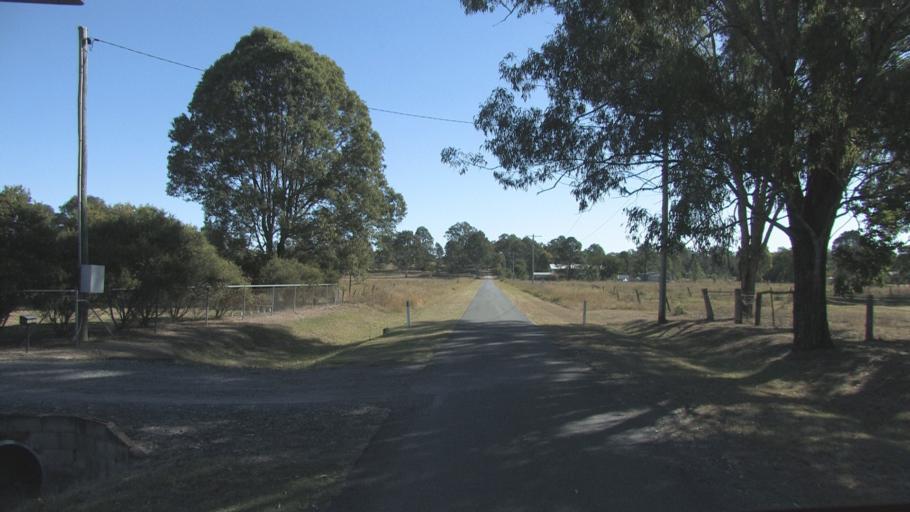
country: AU
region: Queensland
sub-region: Logan
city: North Maclean
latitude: -27.7801
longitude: 153.0218
